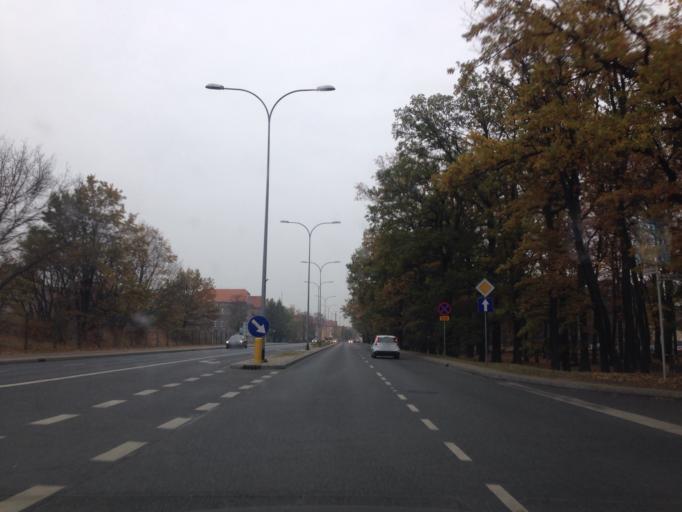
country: PL
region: Kujawsko-Pomorskie
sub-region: Grudziadz
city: Grudziadz
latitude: 53.4710
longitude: 18.7602
